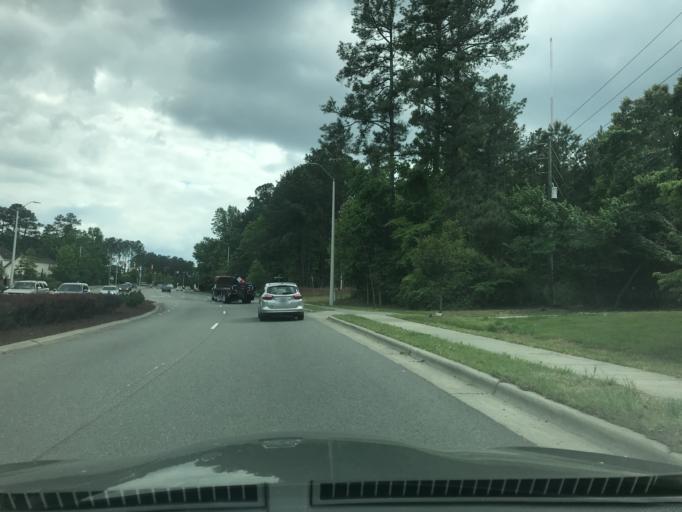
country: US
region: North Carolina
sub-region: Wake County
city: Wake Forest
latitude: 35.9280
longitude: -78.5873
